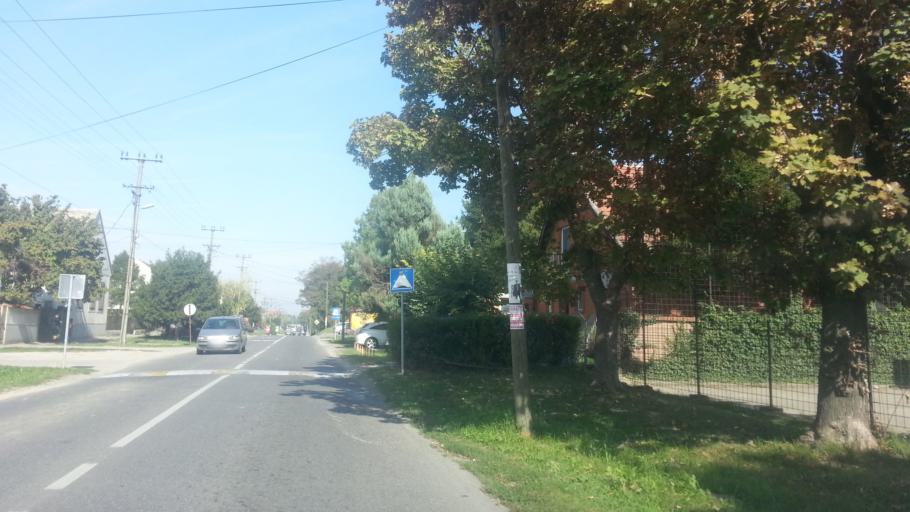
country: RS
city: Stari Banovci
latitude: 44.9855
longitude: 20.2847
